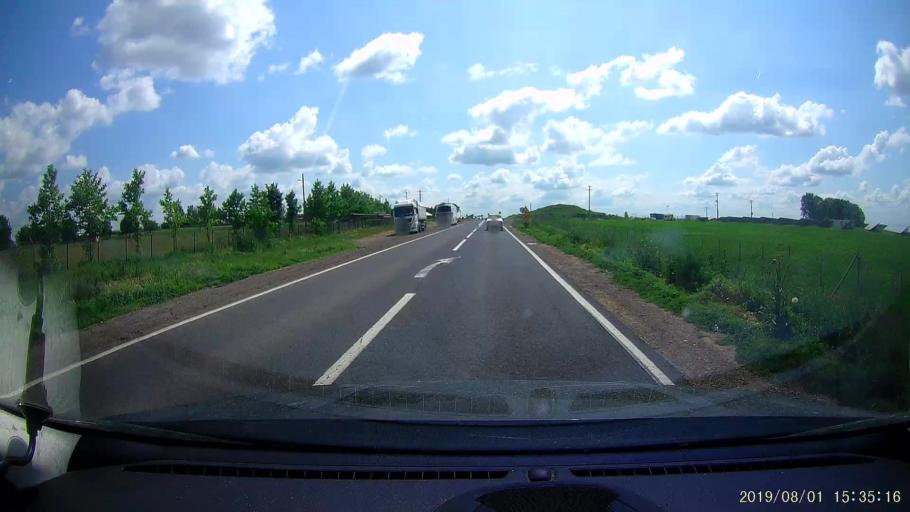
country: RO
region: Braila
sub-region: Comuna Insuratei
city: Insuratei
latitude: 44.9075
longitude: 27.5941
